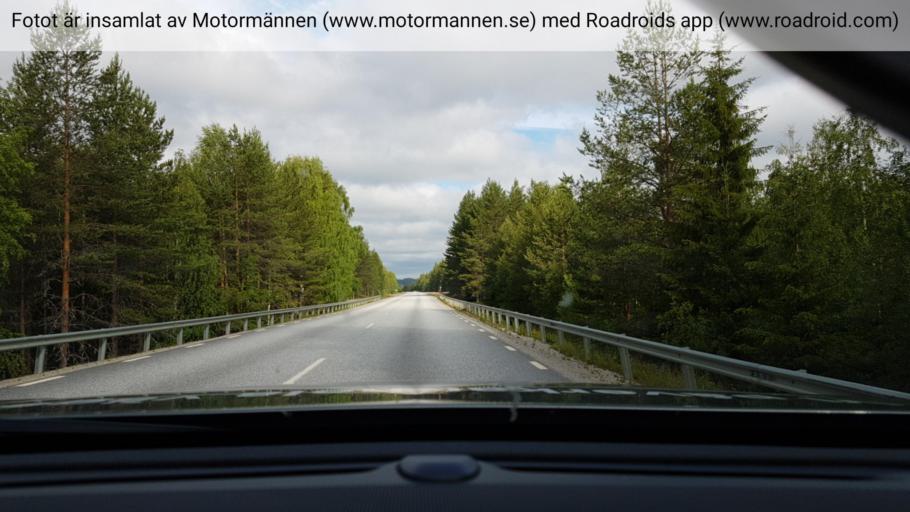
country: SE
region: Vaesterbotten
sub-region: Vindelns Kommun
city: Vindeln
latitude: 64.3762
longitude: 19.4044
